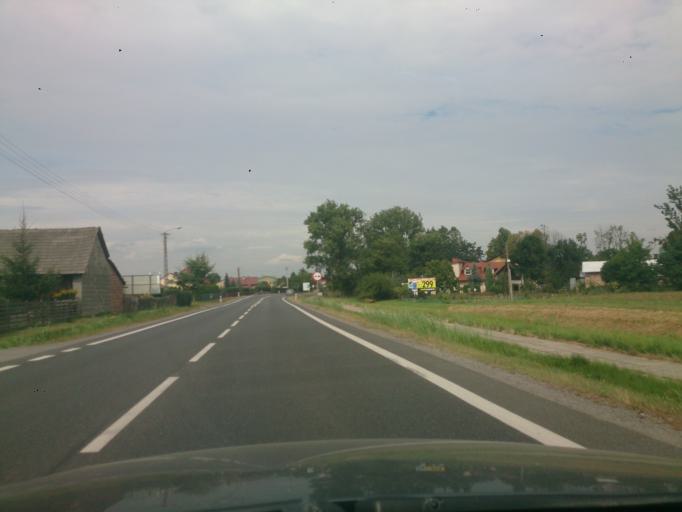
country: PL
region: Subcarpathian Voivodeship
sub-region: Powiat kolbuszowski
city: Kolbuszowa
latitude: 50.2213
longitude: 21.8004
